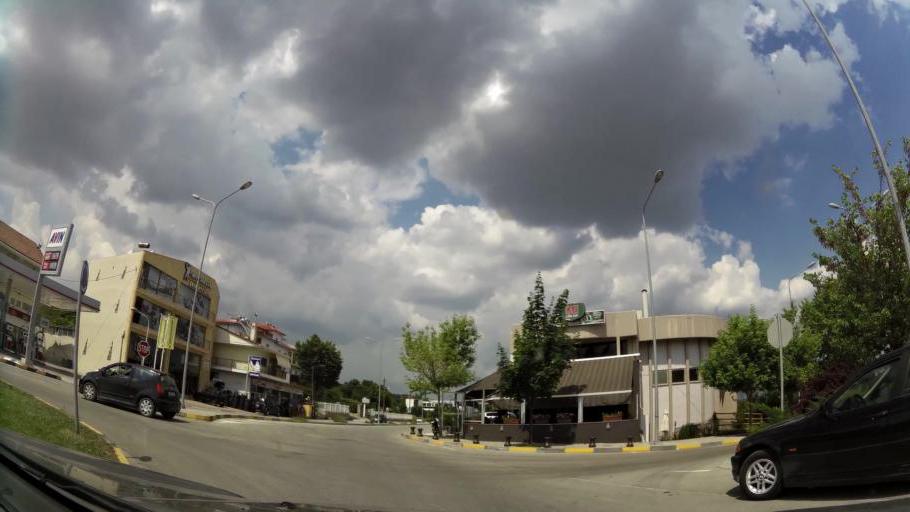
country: GR
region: West Macedonia
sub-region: Nomos Kozanis
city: Kozani
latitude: 40.3038
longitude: 21.8051
